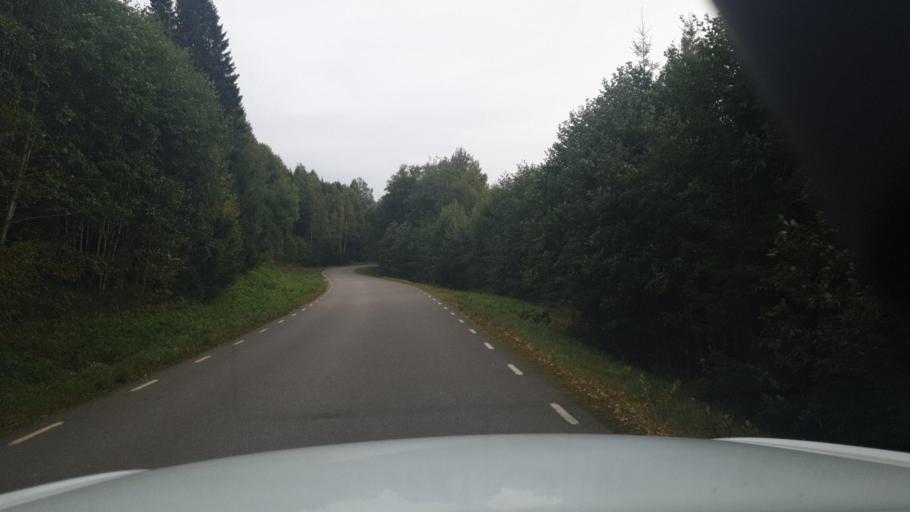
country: SE
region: Vaermland
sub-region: Torsby Kommun
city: Torsby
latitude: 60.0150
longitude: 12.6611
